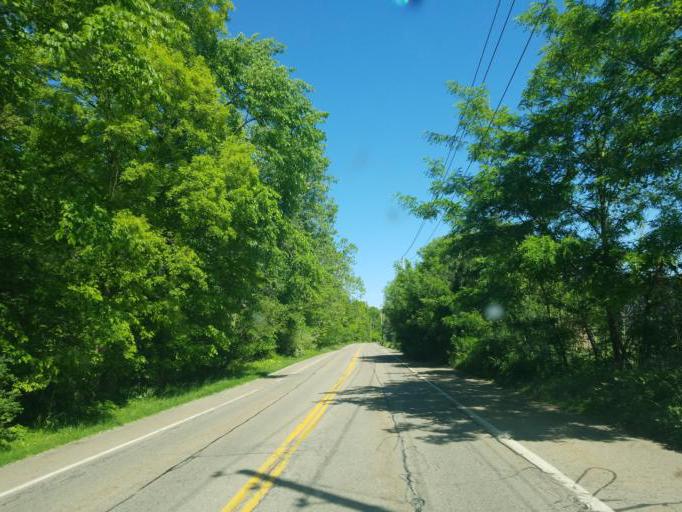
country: US
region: Ohio
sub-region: Summit County
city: Fairlawn
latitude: 41.1532
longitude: -81.5710
